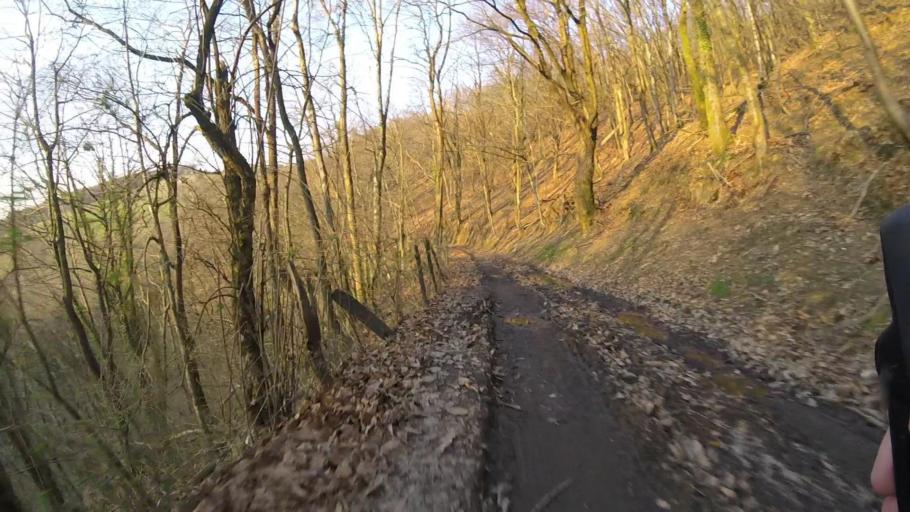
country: ES
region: Basque Country
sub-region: Provincia de Guipuzcoa
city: Errenteria
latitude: 43.2697
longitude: -1.8554
